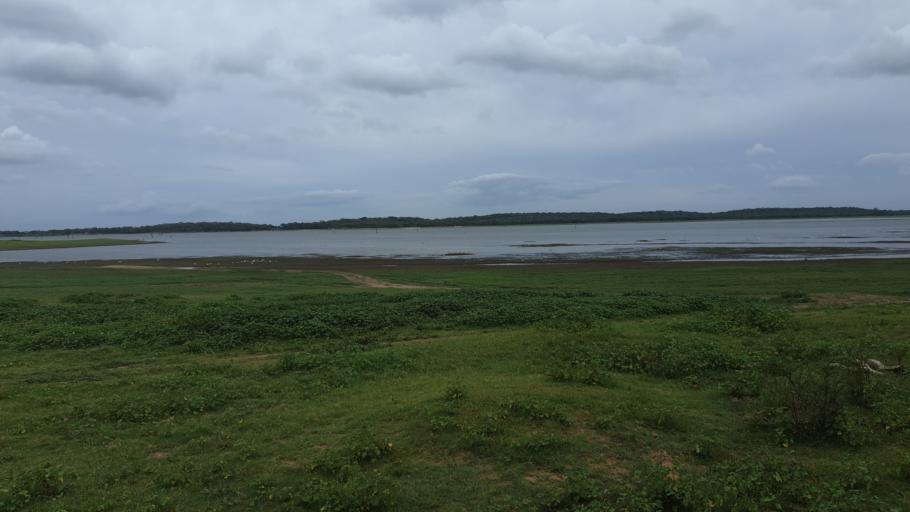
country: LK
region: North Central
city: Polonnaruwa
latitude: 8.1290
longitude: 80.9091
